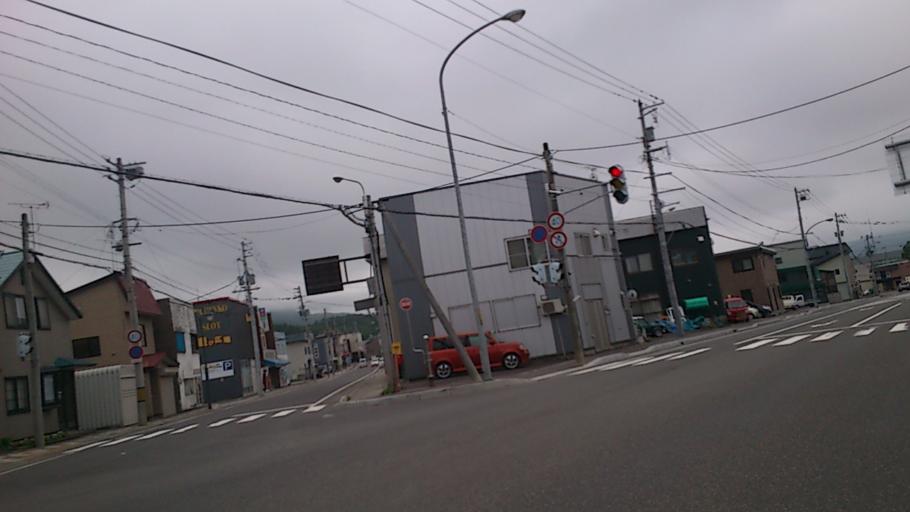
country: JP
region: Hokkaido
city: Niseko Town
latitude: 42.8079
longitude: 140.5296
